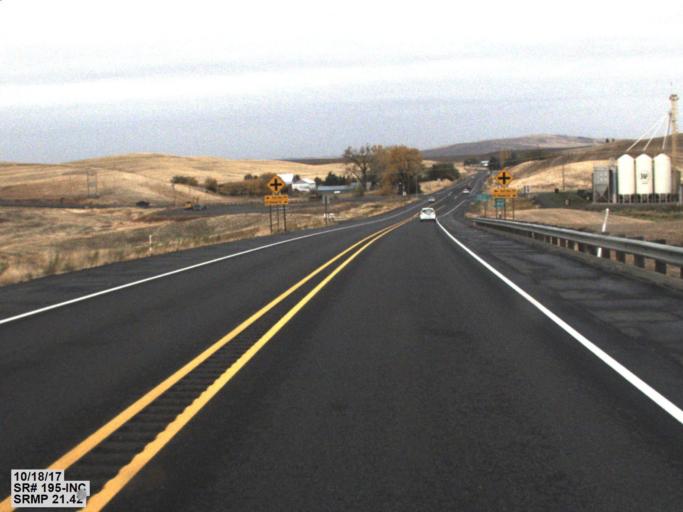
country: US
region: Washington
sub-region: Whitman County
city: Pullman
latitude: 46.7227
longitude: -117.2217
